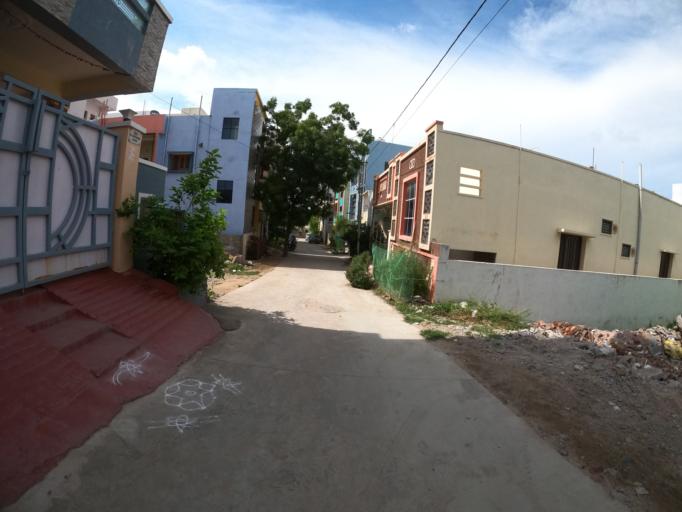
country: IN
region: Telangana
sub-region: Hyderabad
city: Hyderabad
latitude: 17.3673
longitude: 78.3863
